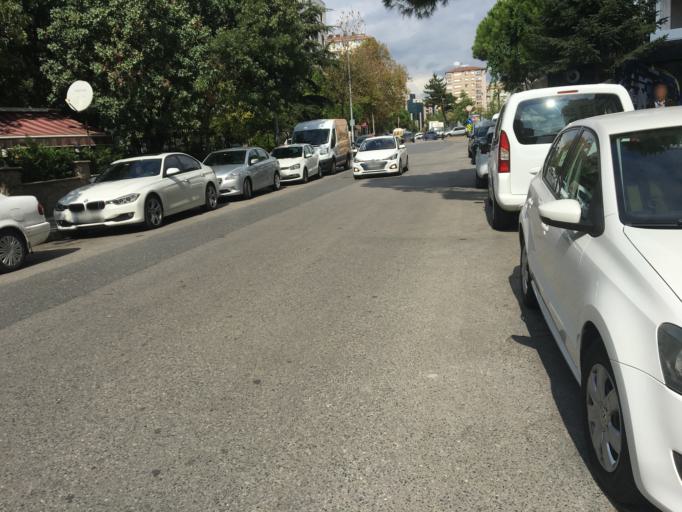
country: TR
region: Istanbul
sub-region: Atasehir
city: Atasehir
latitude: 40.9641
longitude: 29.0981
